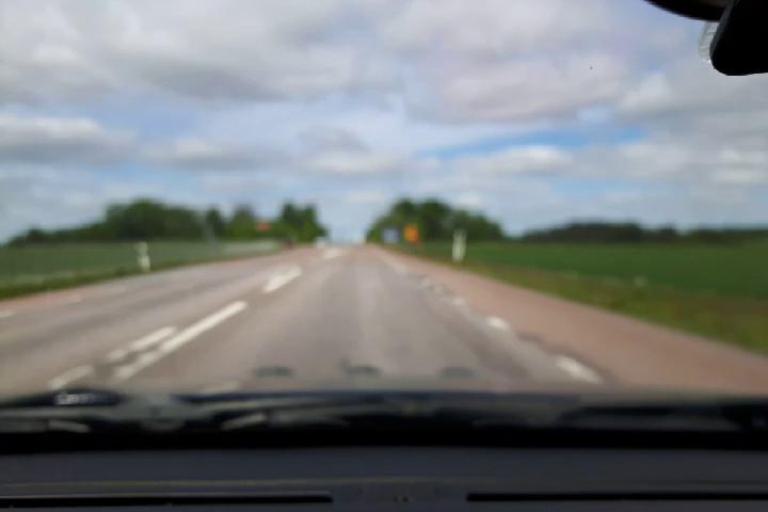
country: SE
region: Uppsala
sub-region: Uppsala Kommun
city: Gamla Uppsala
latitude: 59.9030
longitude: 17.6112
